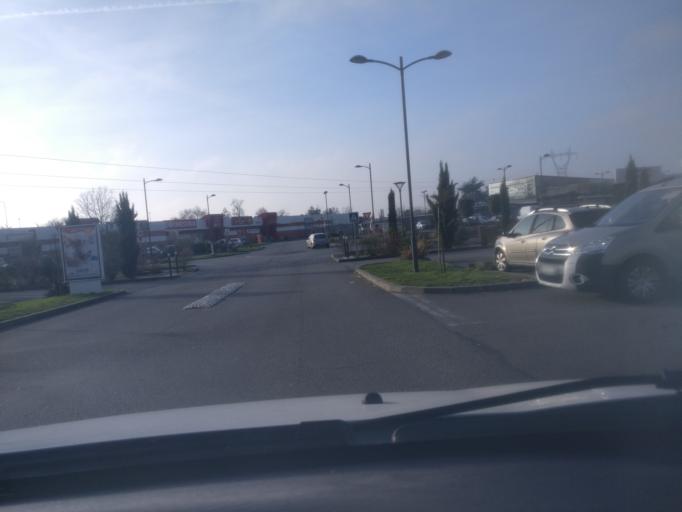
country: FR
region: Pays de la Loire
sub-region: Departement de la Loire-Atlantique
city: Vertou
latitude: 47.1881
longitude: -1.4714
